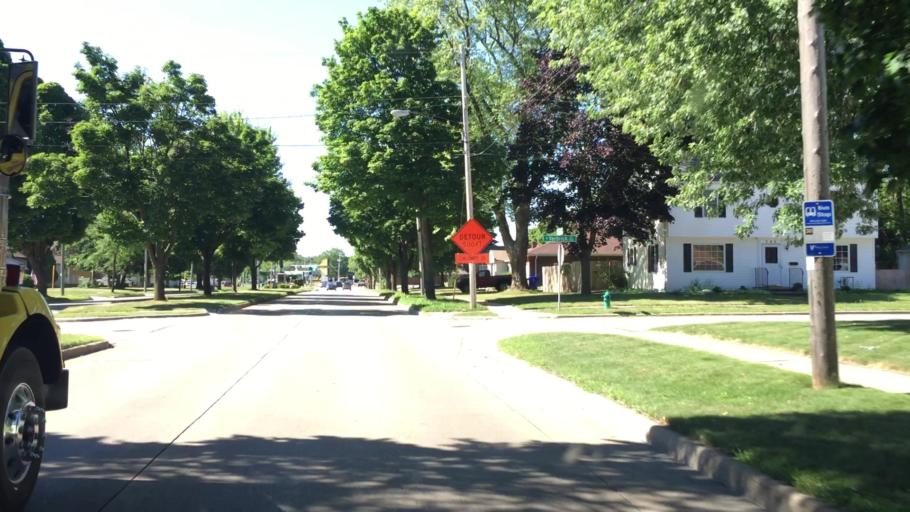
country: US
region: Wisconsin
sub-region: Outagamie County
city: Appleton
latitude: 44.2456
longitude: -88.4157
